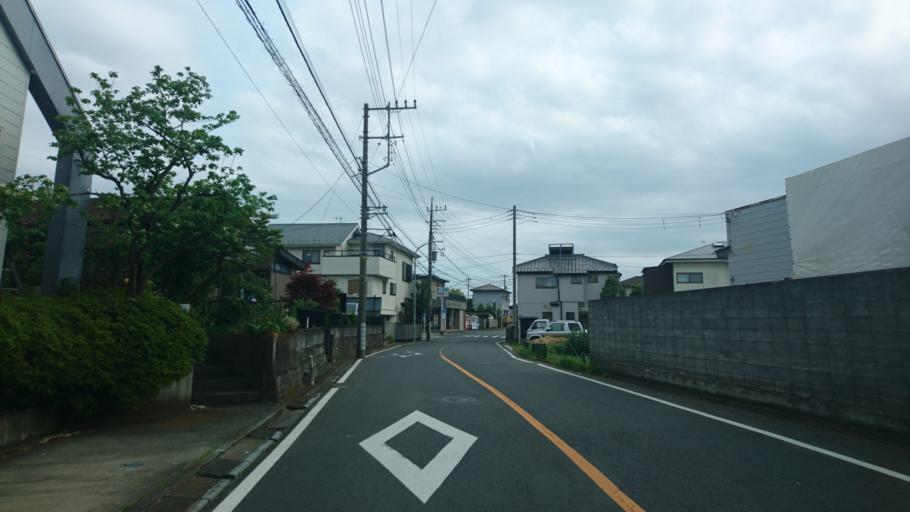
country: JP
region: Kanagawa
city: Fujisawa
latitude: 35.3992
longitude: 139.4798
